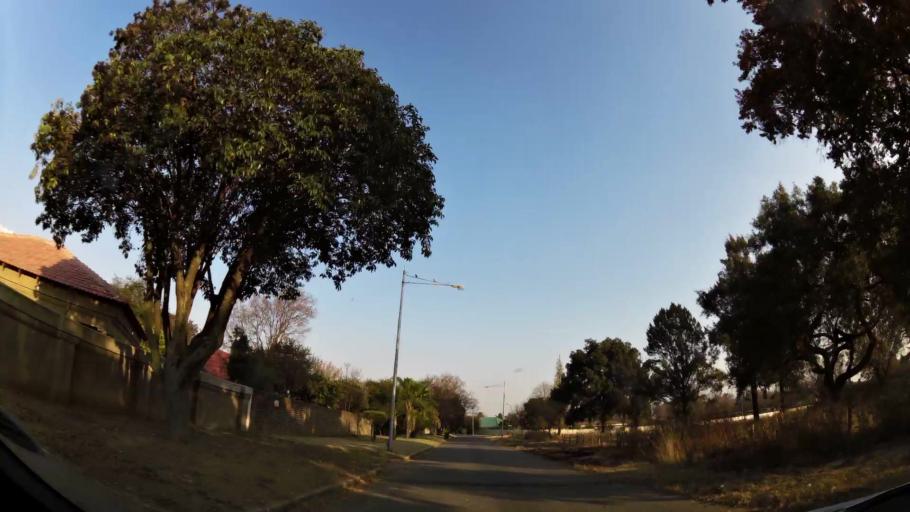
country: ZA
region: Gauteng
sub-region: Ekurhuleni Metropolitan Municipality
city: Springs
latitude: -26.2998
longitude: 28.4516
